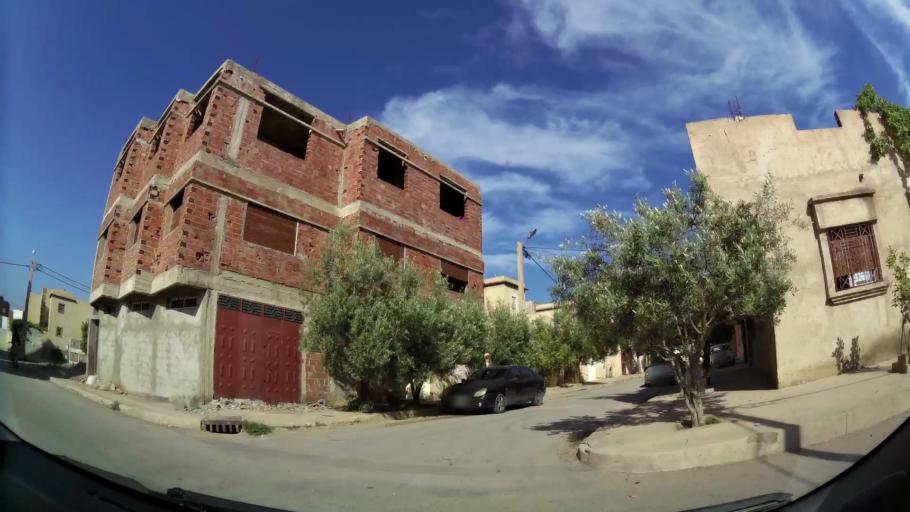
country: MA
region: Oriental
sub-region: Oujda-Angad
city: Oujda
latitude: 34.7188
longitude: -1.8841
